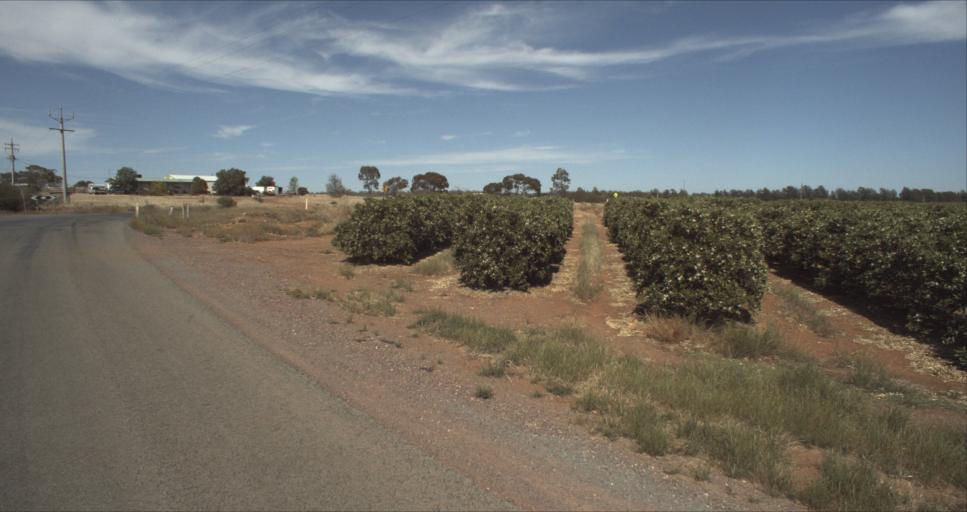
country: AU
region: New South Wales
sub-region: Leeton
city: Leeton
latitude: -34.5925
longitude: 146.4723
